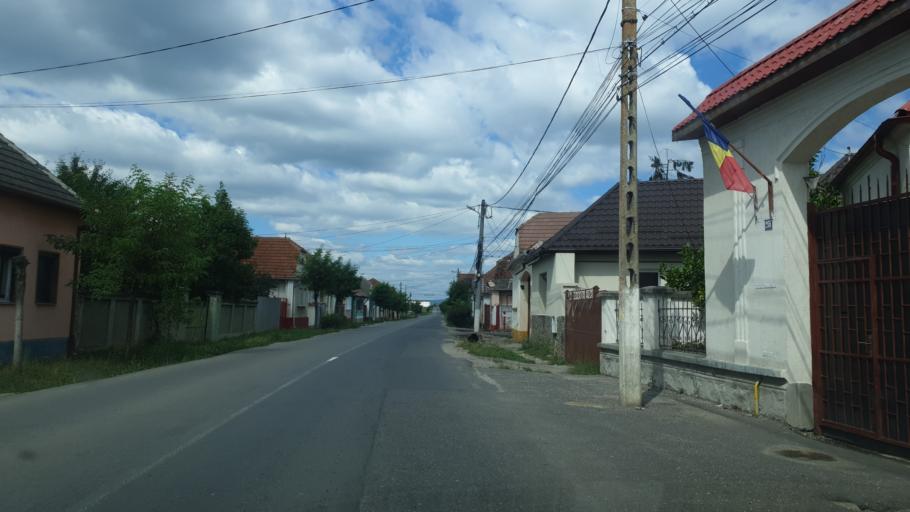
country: RO
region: Brasov
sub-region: Comuna Sanpetru
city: Sanpetru
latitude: 45.7178
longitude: 25.6275
